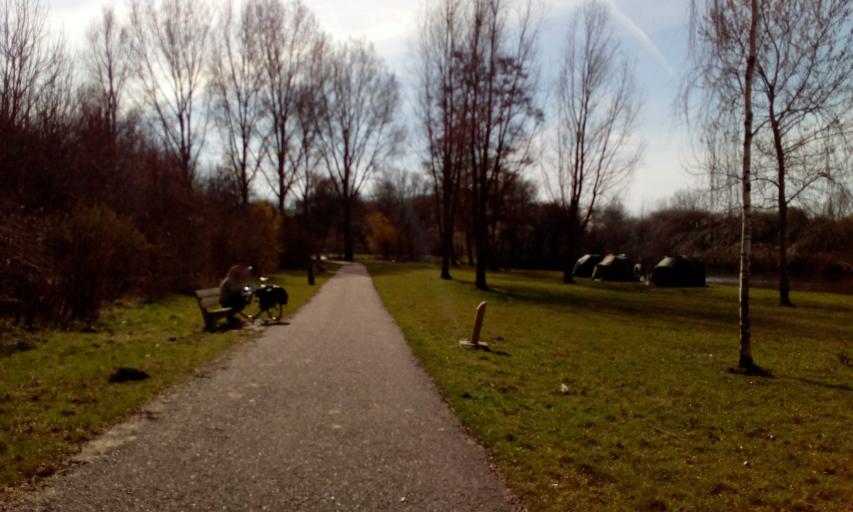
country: NL
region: South Holland
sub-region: Gemeente Lansingerland
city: Bergschenhoek
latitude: 51.9636
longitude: 4.5260
